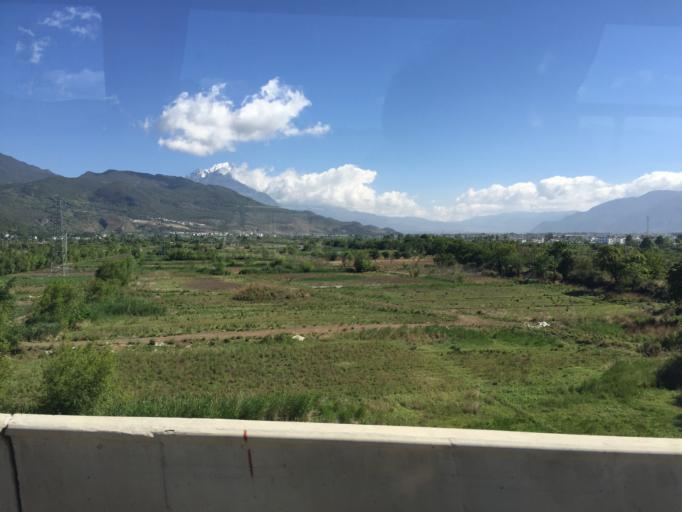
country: CN
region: Yunnan
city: Lijiang
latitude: 26.8842
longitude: 100.1932
